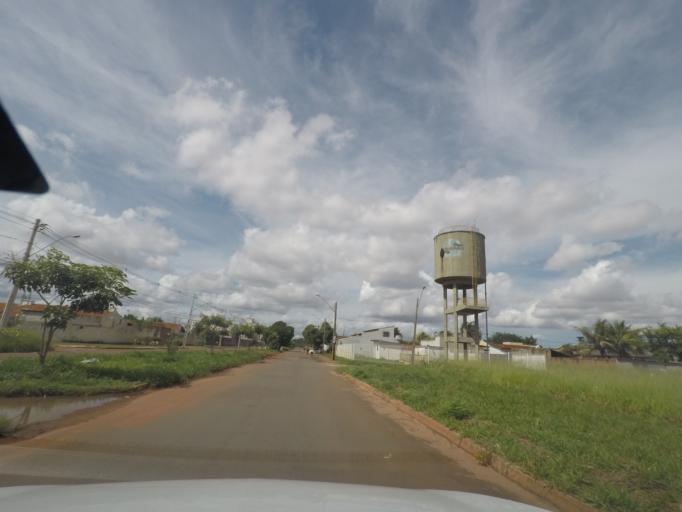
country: BR
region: Goias
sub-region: Goiania
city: Goiania
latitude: -16.7194
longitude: -49.3478
